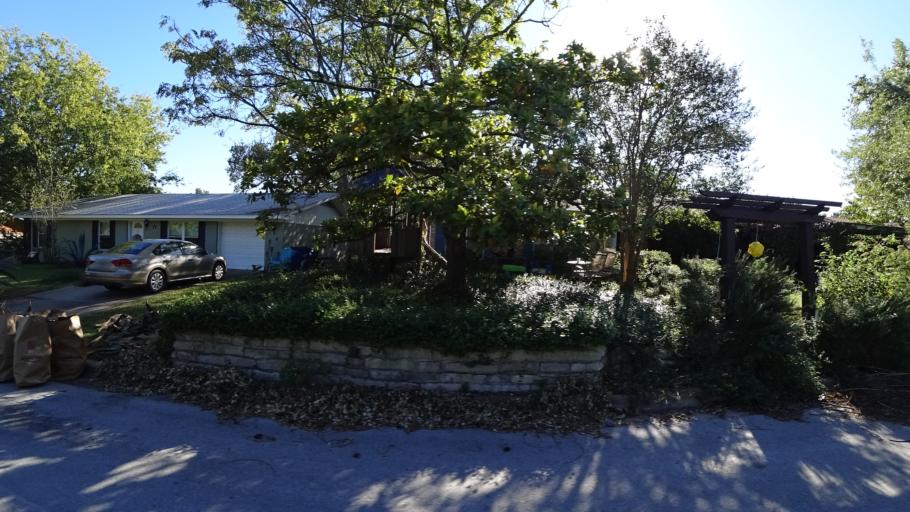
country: US
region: Texas
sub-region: Travis County
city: Rollingwood
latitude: 30.2365
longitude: -97.8076
